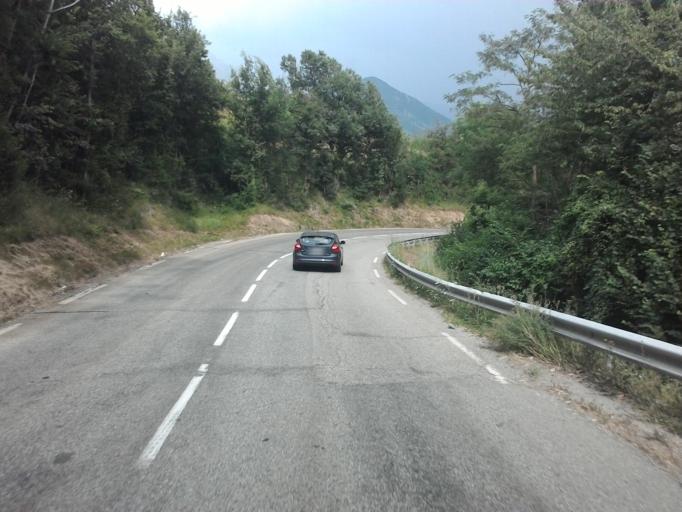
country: FR
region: Rhone-Alpes
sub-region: Departement de l'Isere
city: La Mure
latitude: 44.9002
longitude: 5.8108
